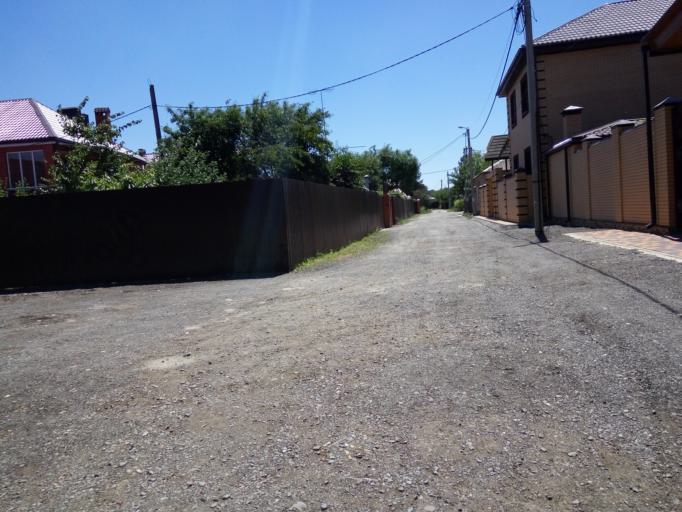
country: RU
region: Rostov
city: Bataysk
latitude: 47.1481
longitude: 39.7696
